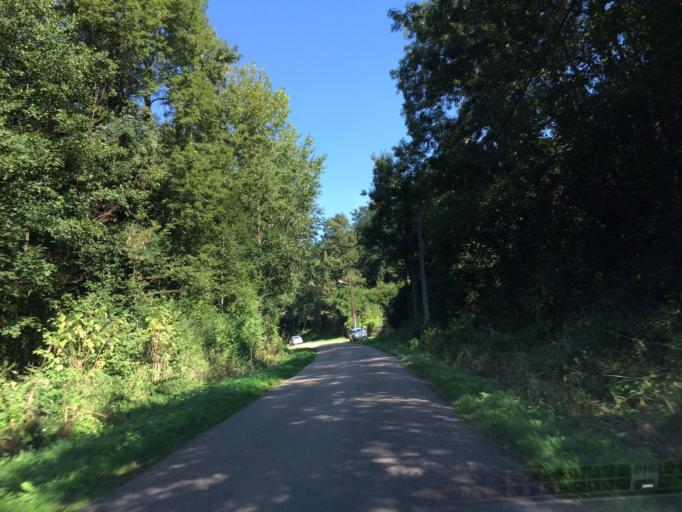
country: FR
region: Bourgogne
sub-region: Departement de l'Yonne
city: Fleury-la-Vallee
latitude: 47.8523
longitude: 3.3998
